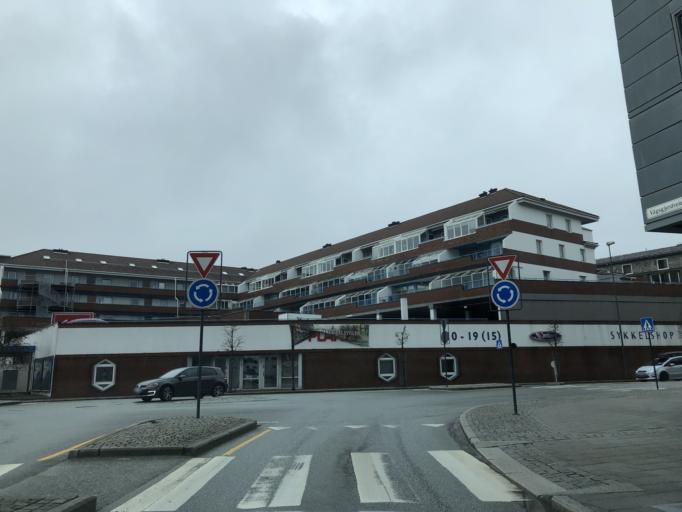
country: NO
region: Rogaland
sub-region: Sandnes
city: Sandnes
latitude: 58.8494
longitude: 5.7373
